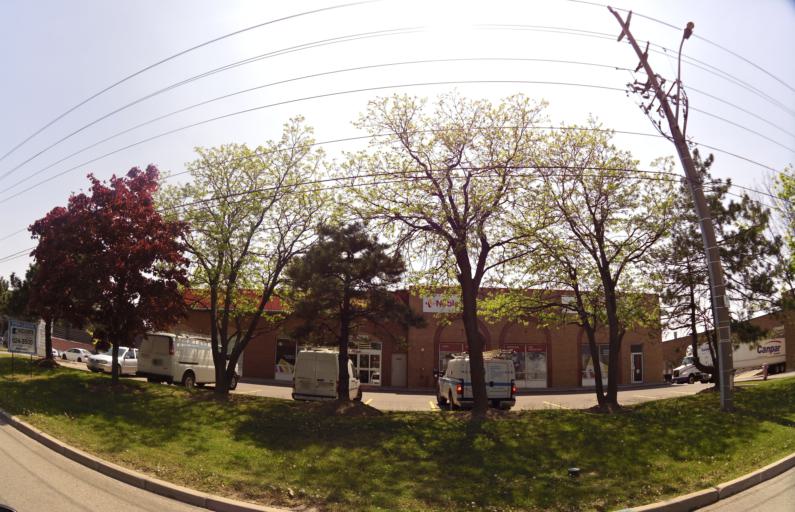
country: CA
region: Ontario
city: Mississauga
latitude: 43.6432
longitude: -79.6371
